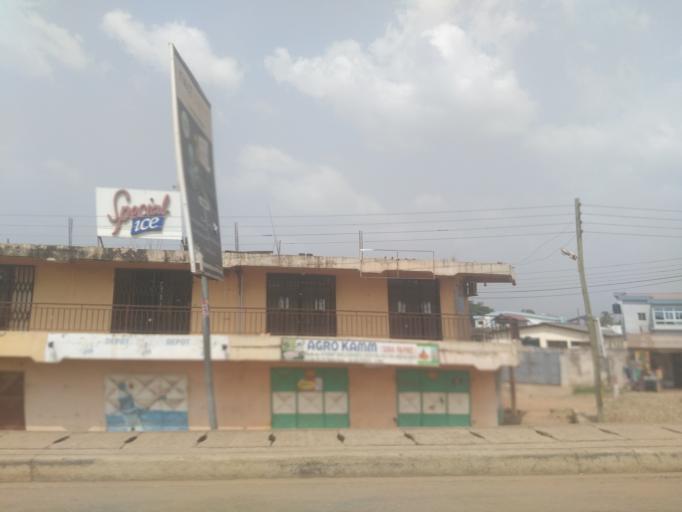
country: GH
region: Greater Accra
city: Gbawe
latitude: 5.6009
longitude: -0.2616
